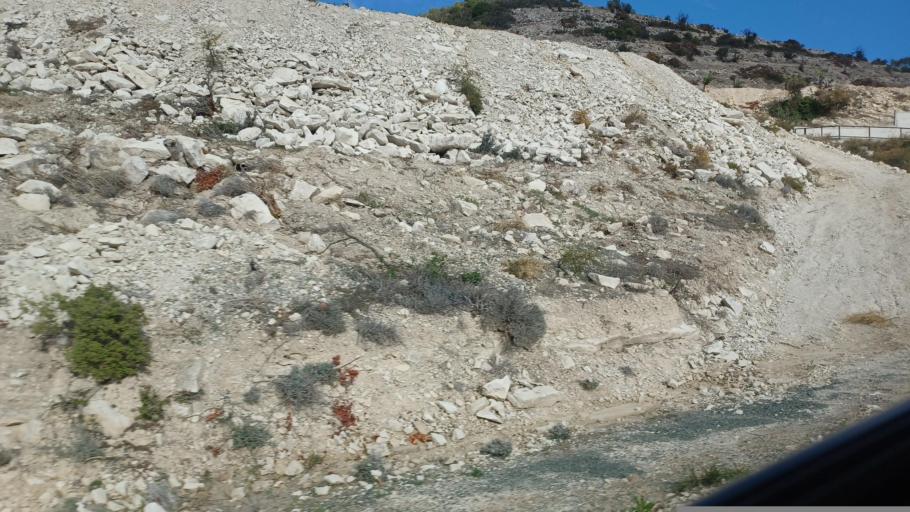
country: CY
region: Limassol
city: Pano Polemidia
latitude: 34.7936
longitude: 32.9856
